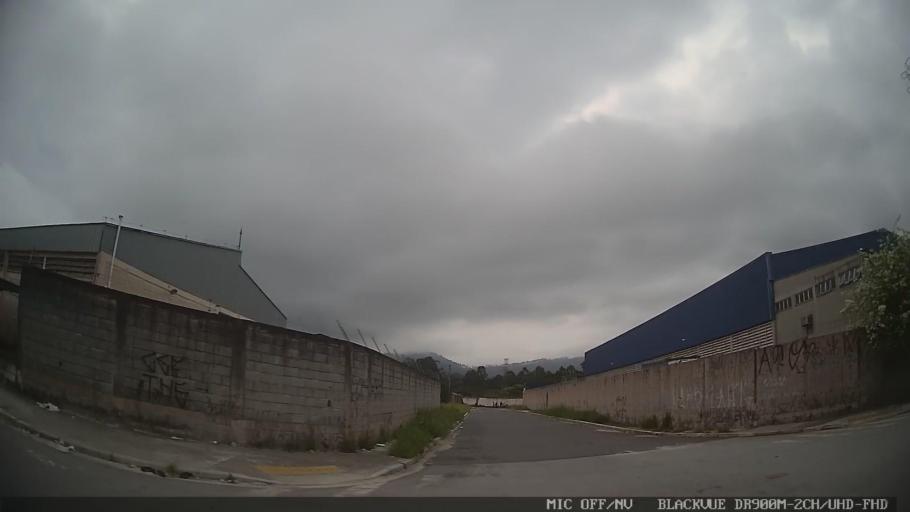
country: BR
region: Sao Paulo
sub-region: Mogi das Cruzes
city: Mogi das Cruzes
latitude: -23.5296
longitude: -46.2199
